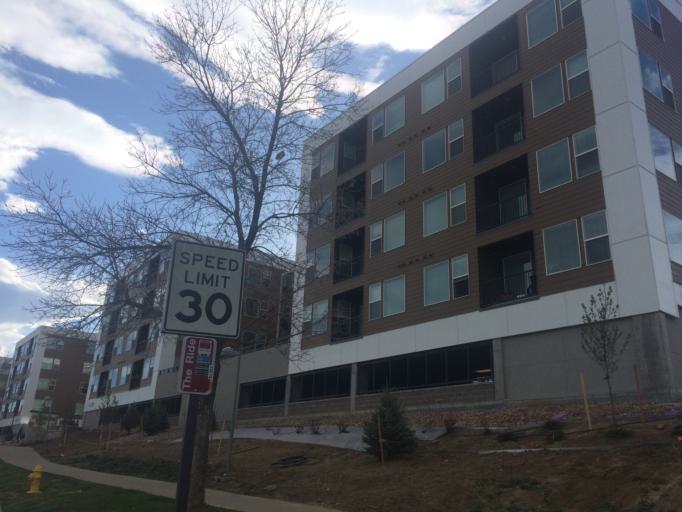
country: US
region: Colorado
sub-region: Broomfield County
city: Broomfield
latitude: 39.9235
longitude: -105.1214
